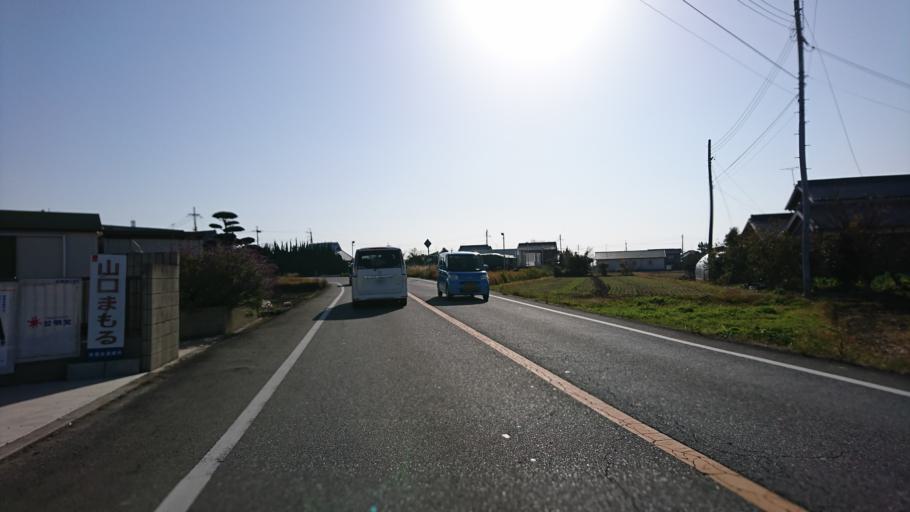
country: JP
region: Hyogo
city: Kakogawacho-honmachi
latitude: 34.7625
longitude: 134.9100
